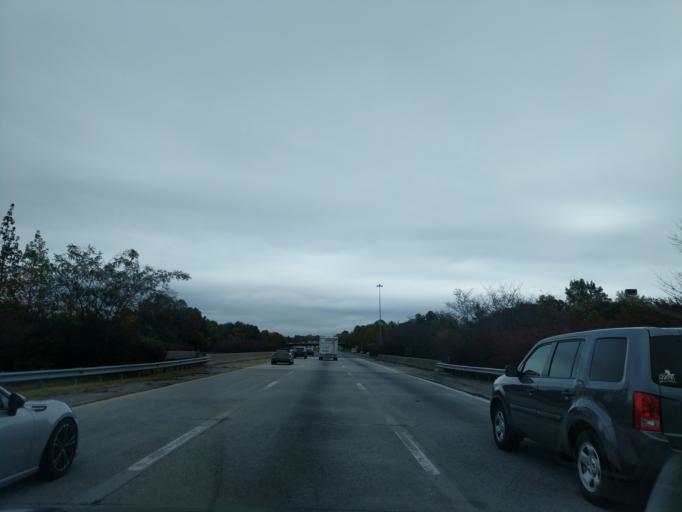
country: US
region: North Carolina
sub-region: Davidson County
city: Thomasville
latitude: 35.8604
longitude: -80.0747
